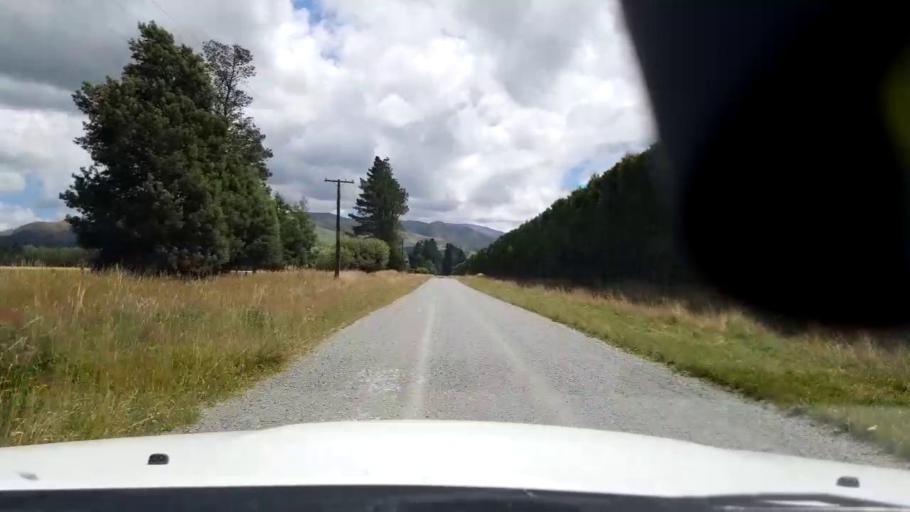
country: NZ
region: Canterbury
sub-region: Timaru District
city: Pleasant Point
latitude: -43.9708
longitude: 171.2407
